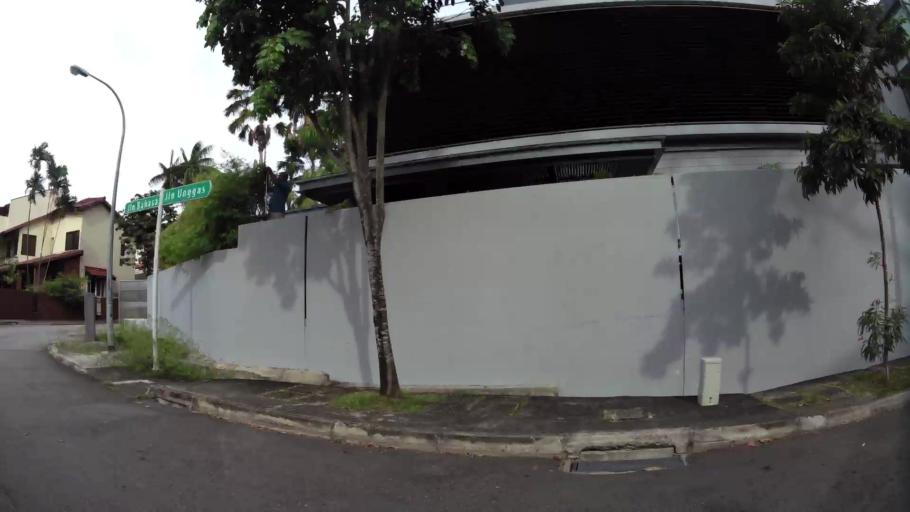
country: SG
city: Singapore
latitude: 1.3262
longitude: 103.8181
